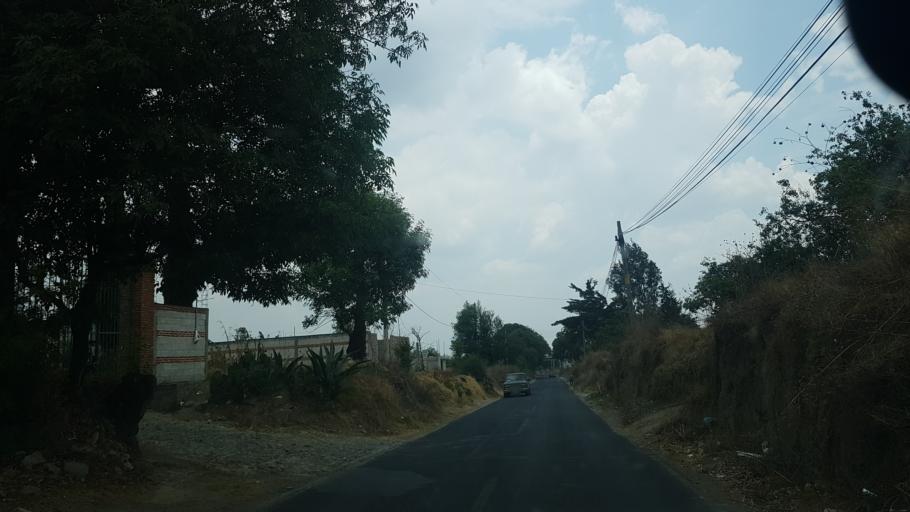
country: MX
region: Puebla
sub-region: Huejotzingo
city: San Miguel Tianguizolco
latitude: 19.1592
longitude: -98.4278
